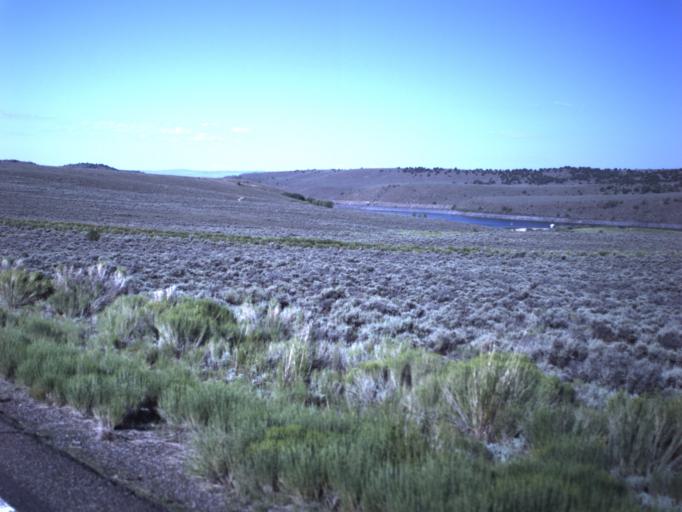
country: US
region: Utah
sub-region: Wayne County
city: Loa
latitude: 38.5217
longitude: -111.5208
